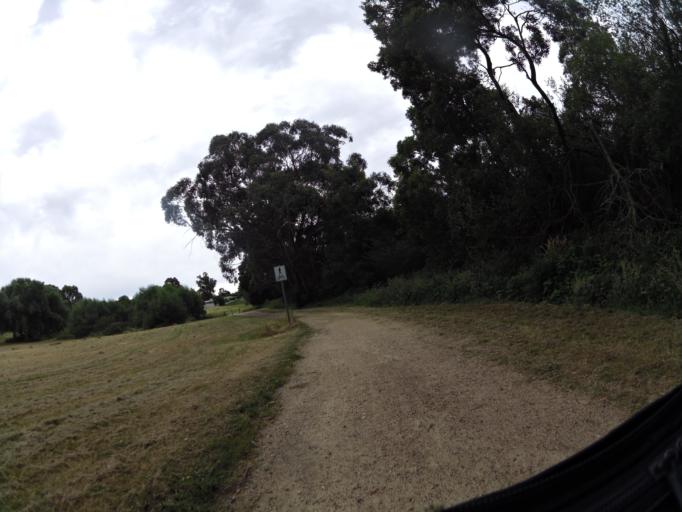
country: AU
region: Victoria
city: Brown Hill
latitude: -37.4302
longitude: 143.9008
